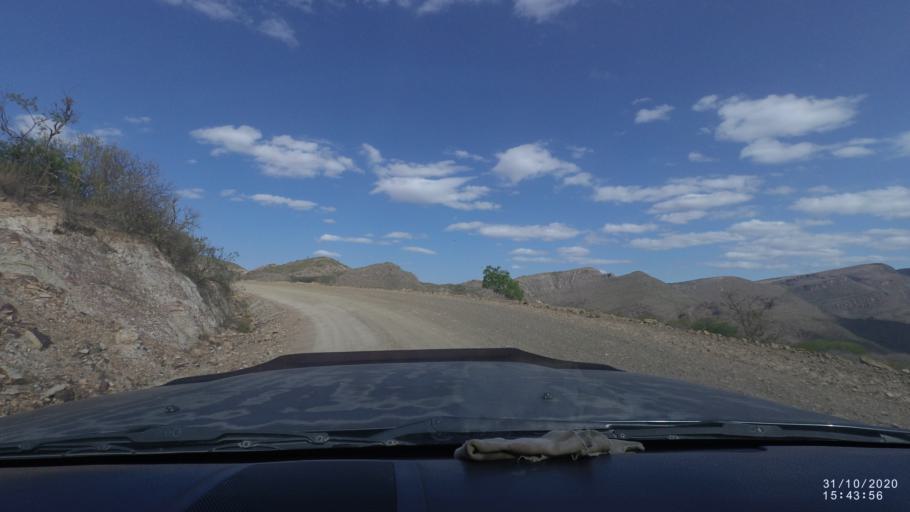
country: BO
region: Chuquisaca
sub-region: Provincia Zudanez
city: Mojocoya
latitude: -18.3198
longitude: -64.7261
